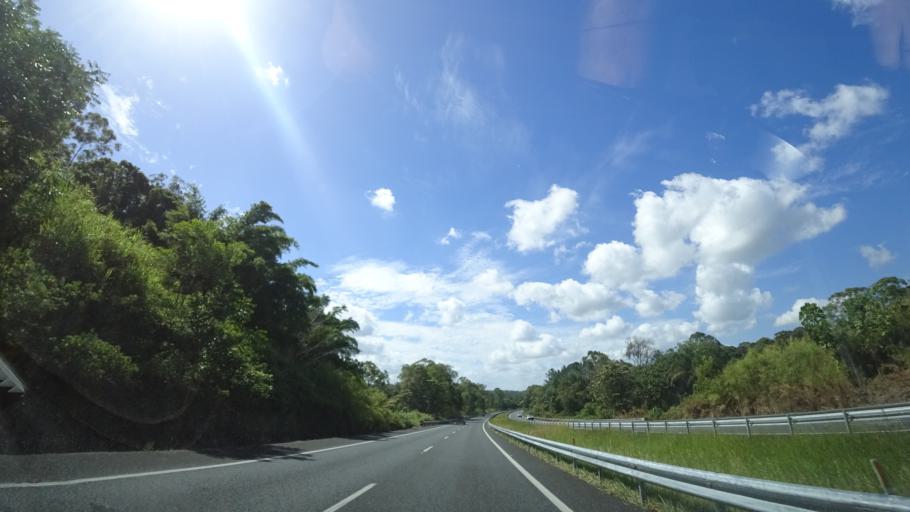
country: AU
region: Queensland
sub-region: Sunshine Coast
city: Woombye
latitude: -26.6538
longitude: 152.9914
